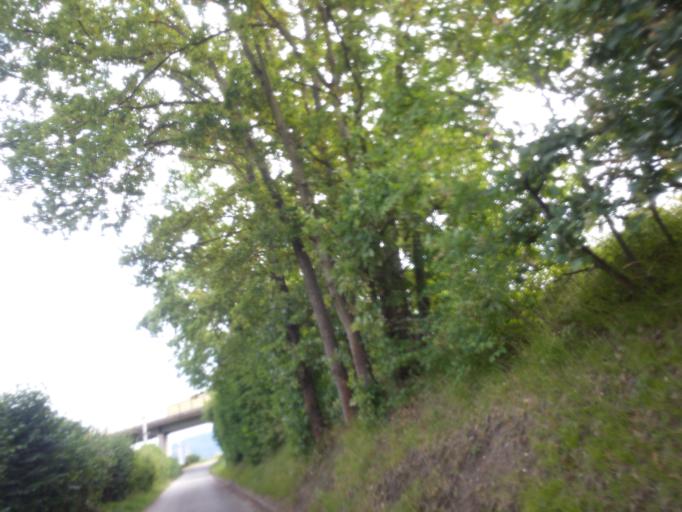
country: AT
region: Carinthia
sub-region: Politischer Bezirk Klagenfurt Land
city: Maria Worth
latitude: 46.6323
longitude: 14.1616
